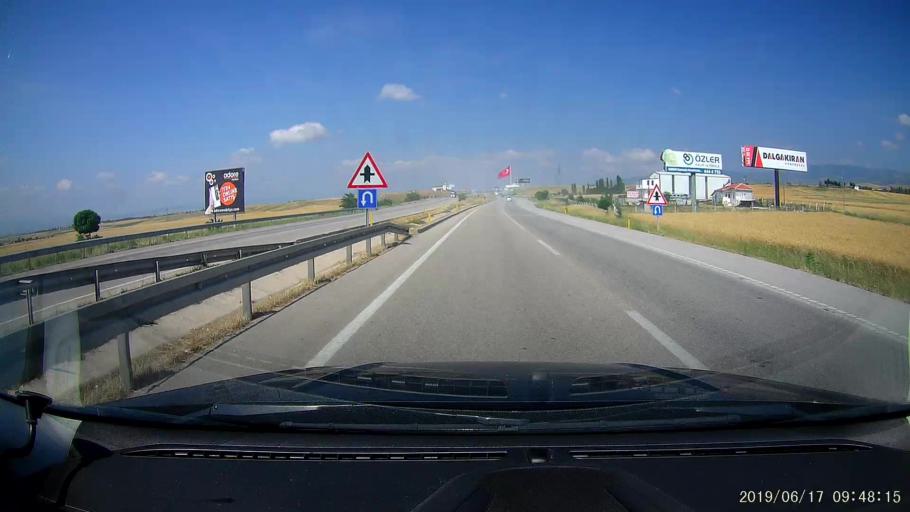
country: TR
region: Amasya
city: Merzifon
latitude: 40.8750
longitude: 35.5579
